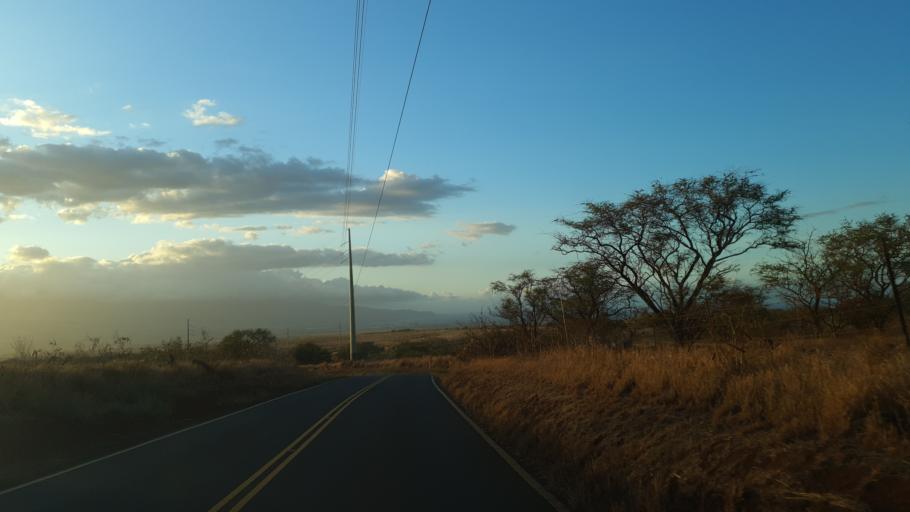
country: US
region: Hawaii
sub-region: Maui County
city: Pukalani
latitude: 20.8017
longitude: -156.3751
